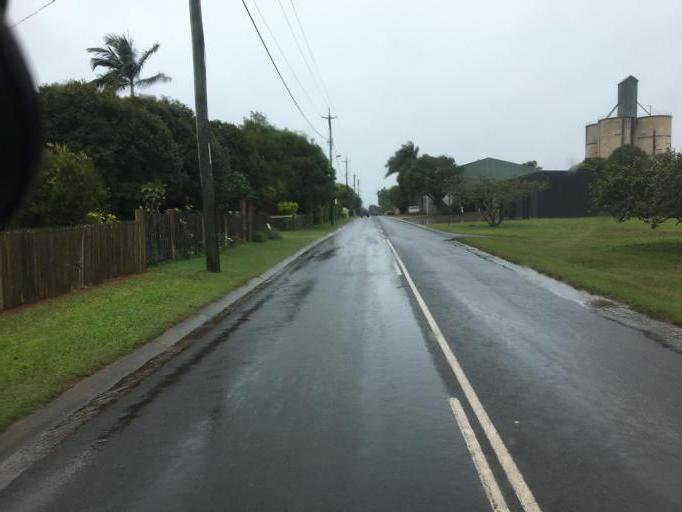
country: AU
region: Queensland
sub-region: Tablelands
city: Tolga
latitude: -17.2156
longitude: 145.5391
